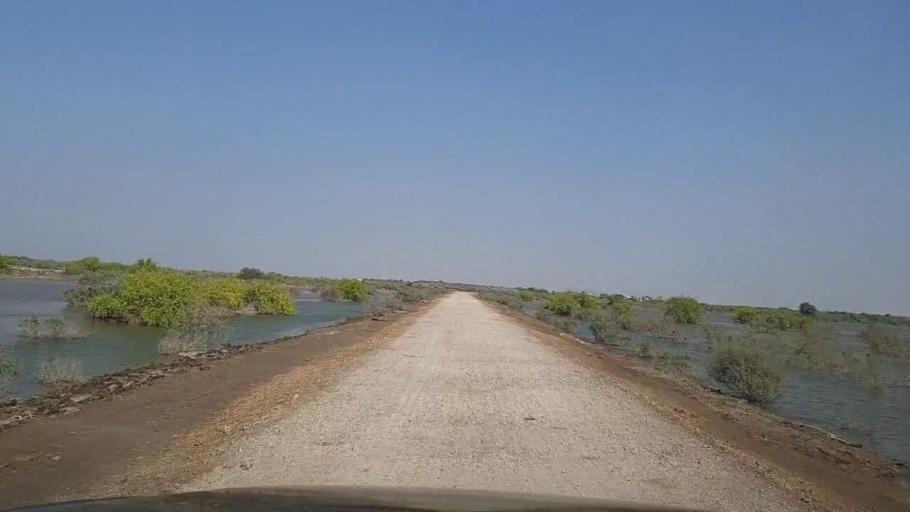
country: PK
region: Sindh
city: Thatta
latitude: 24.6428
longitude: 67.8154
